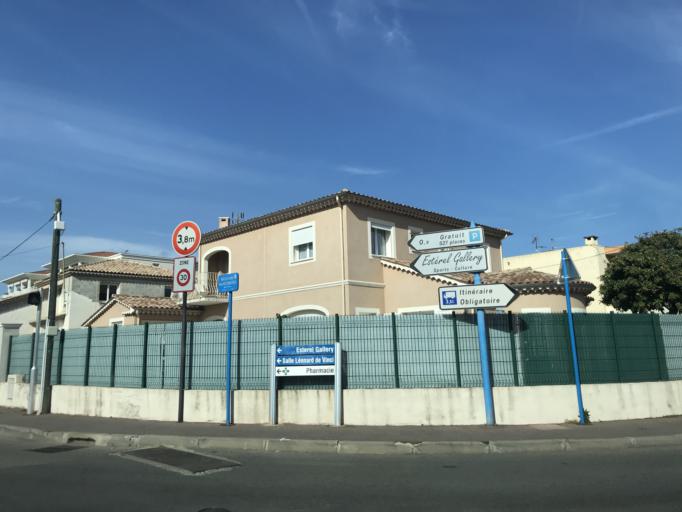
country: FR
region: Provence-Alpes-Cote d'Azur
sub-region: Departement des Alpes-Maritimes
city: Mandelieu-la-Napoule
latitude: 43.5389
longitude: 6.9414
